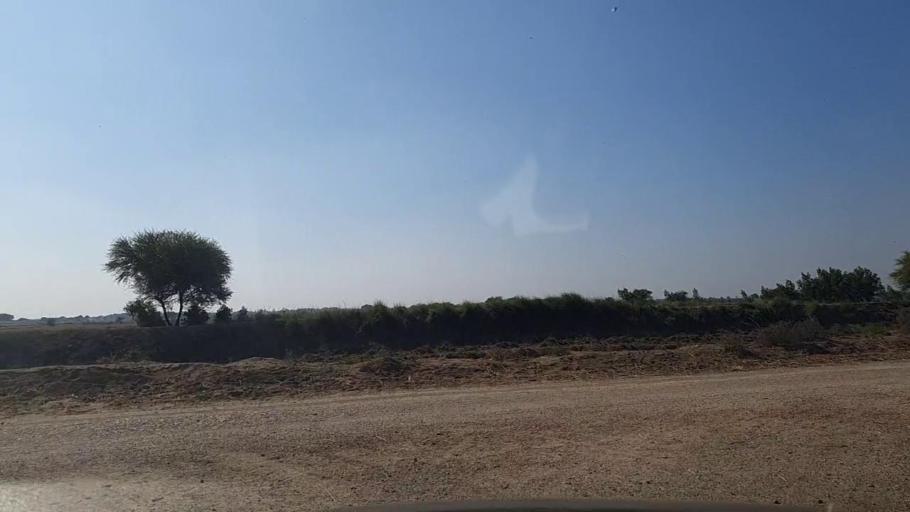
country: PK
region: Sindh
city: Mirpur Batoro
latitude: 24.7258
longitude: 68.2315
